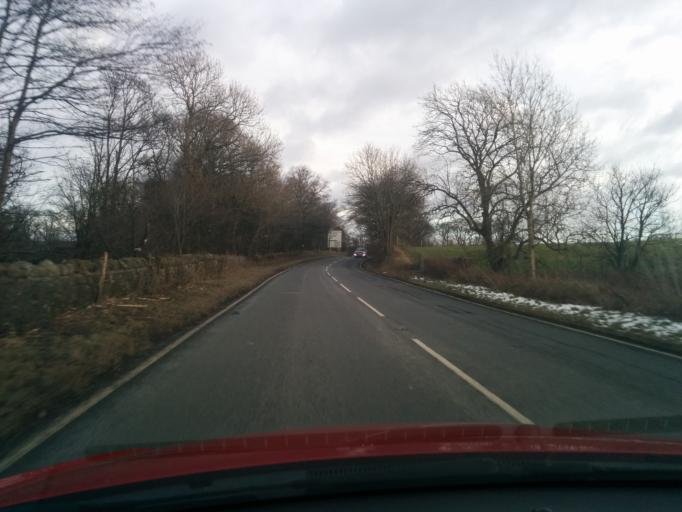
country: GB
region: Scotland
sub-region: Fife
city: Limekilns
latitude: 55.9843
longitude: -3.5156
